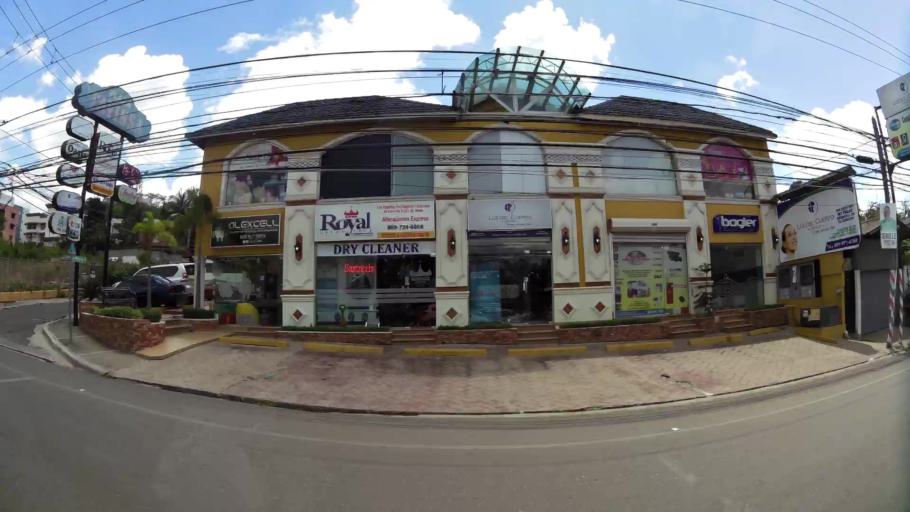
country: DO
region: Santiago
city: Santiago de los Caballeros
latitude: 19.4698
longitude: -70.6847
